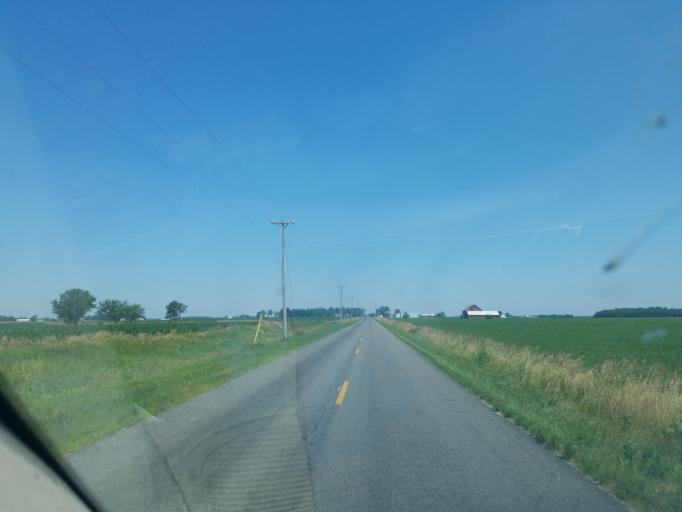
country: US
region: Ohio
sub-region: Mercer County
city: Rockford
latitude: 40.6425
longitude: -84.7086
